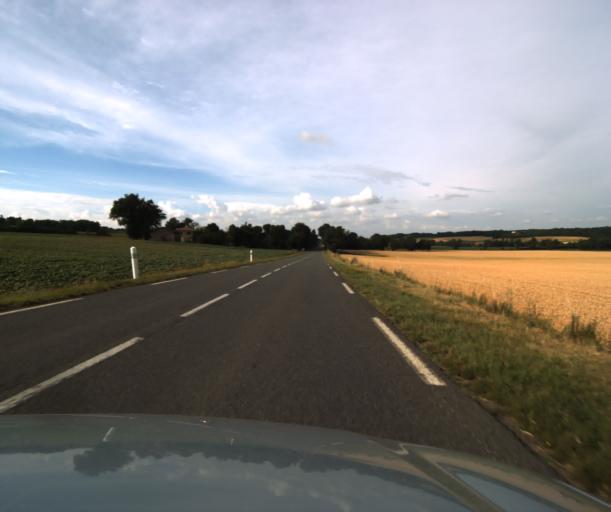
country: FR
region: Midi-Pyrenees
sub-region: Departement du Tarn-et-Garonne
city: Beaumont-de-Lomagne
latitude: 43.7787
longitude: 0.8872
